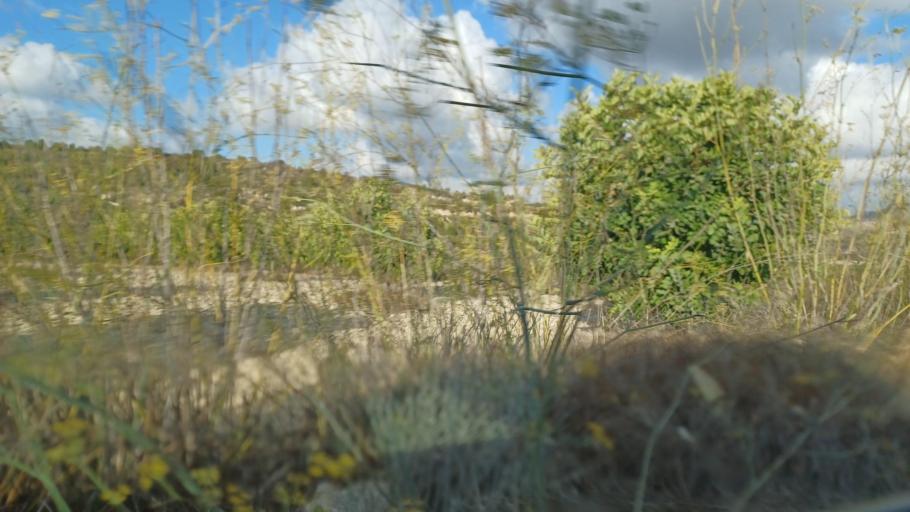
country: CY
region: Pafos
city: Mesogi
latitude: 34.8663
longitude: 32.4954
